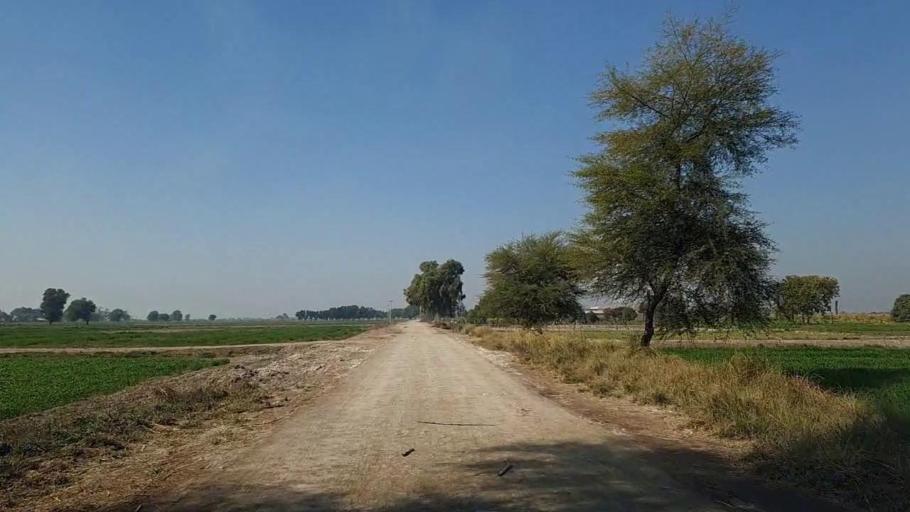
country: PK
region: Sindh
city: Nawabshah
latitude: 26.2823
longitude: 68.3832
